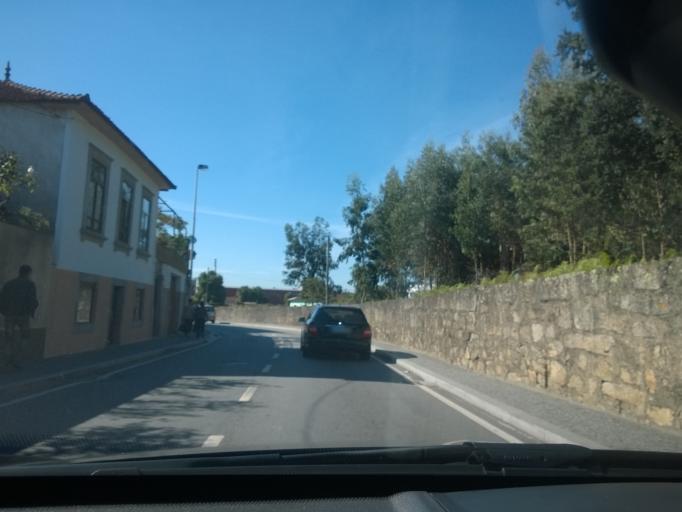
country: PT
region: Porto
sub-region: Maia
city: Gemunde
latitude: 41.2468
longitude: -8.6643
